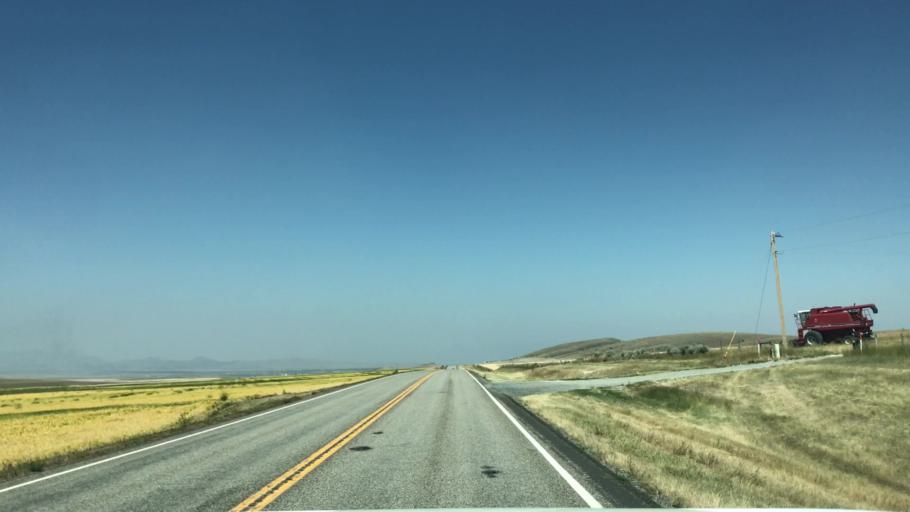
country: US
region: Montana
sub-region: Gallatin County
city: Three Forks
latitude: 46.0053
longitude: -111.5845
